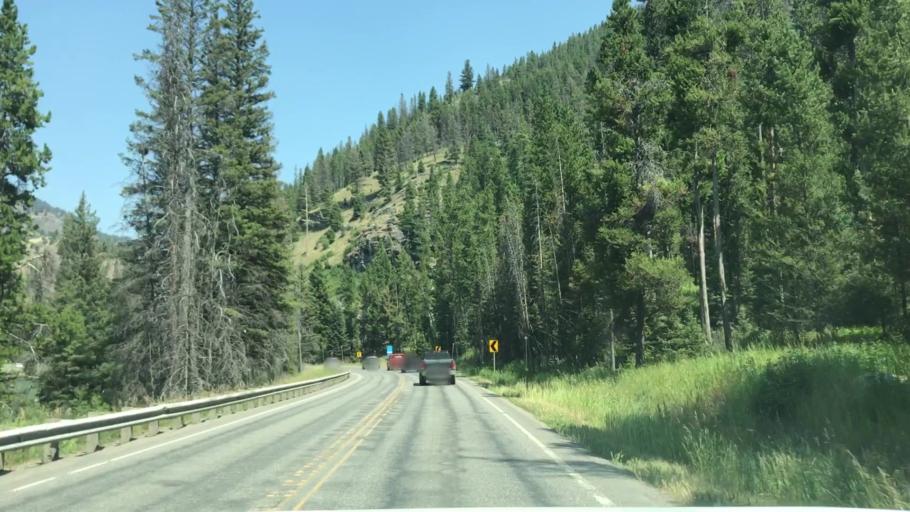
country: US
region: Montana
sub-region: Gallatin County
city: Big Sky
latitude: 45.3021
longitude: -111.1976
